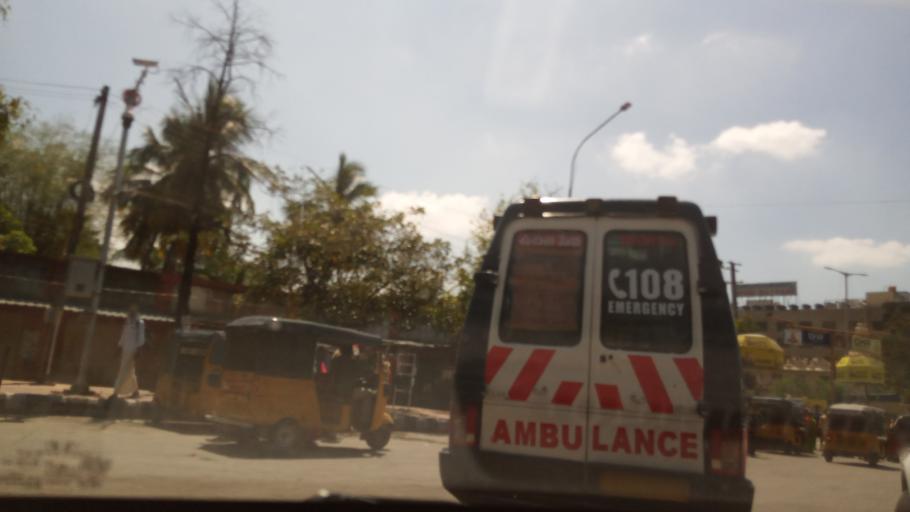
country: IN
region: Andhra Pradesh
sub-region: Chittoor
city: Akkarampalle
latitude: 13.6541
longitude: 79.4205
